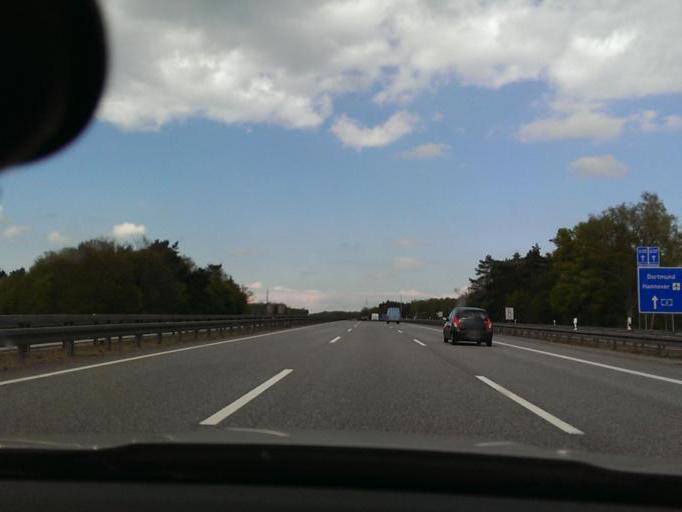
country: DE
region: Lower Saxony
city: Lehrte
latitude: 52.3933
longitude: 9.9000
